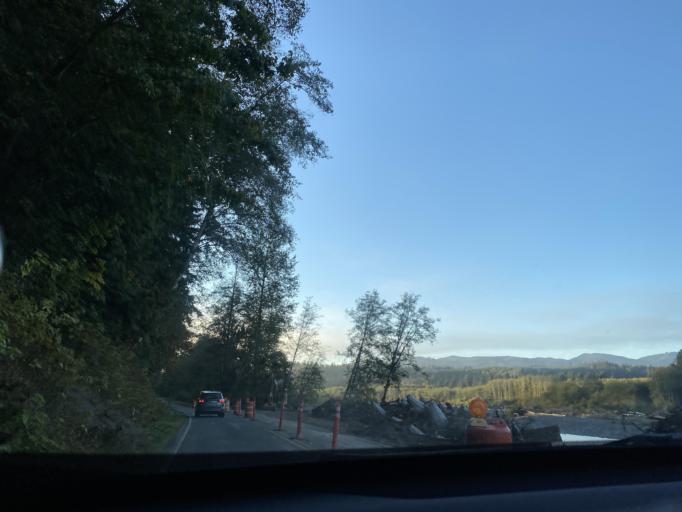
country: US
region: Washington
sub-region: Clallam County
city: Forks
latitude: 47.8212
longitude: -124.1808
